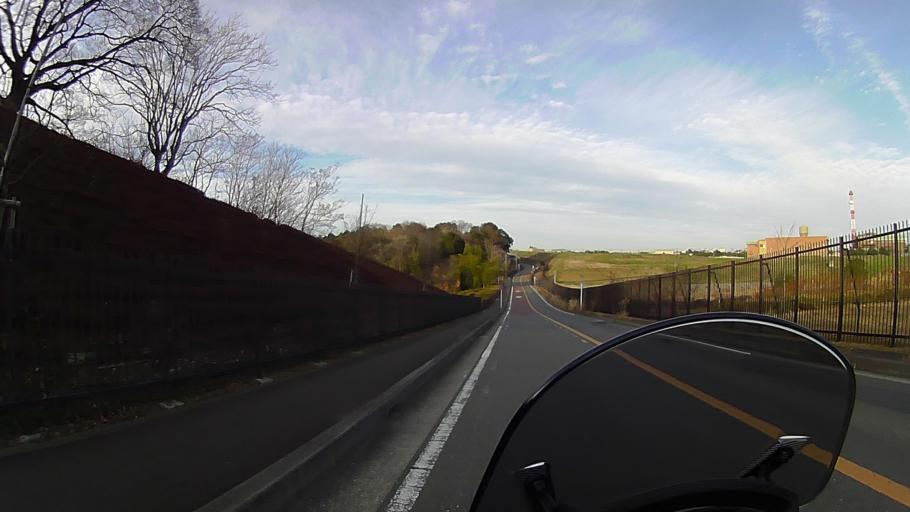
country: JP
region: Kanagawa
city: Atsugi
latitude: 35.4189
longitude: 139.4169
